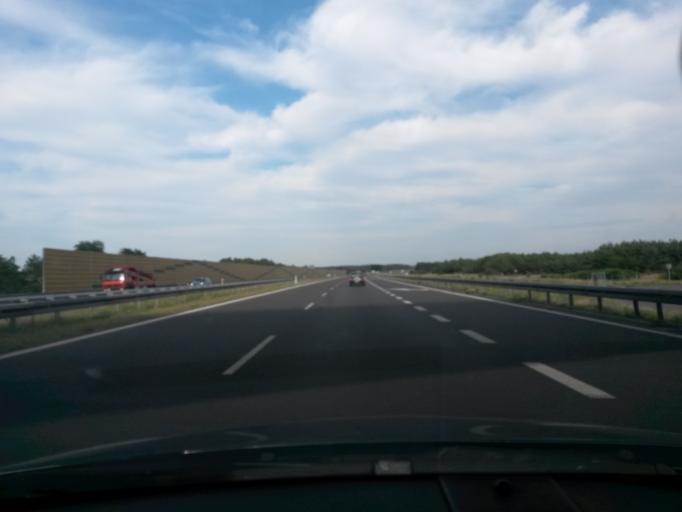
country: PL
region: Greater Poland Voivodeship
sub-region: Powiat koninski
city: Krzymow
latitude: 52.1524
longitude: 18.4602
